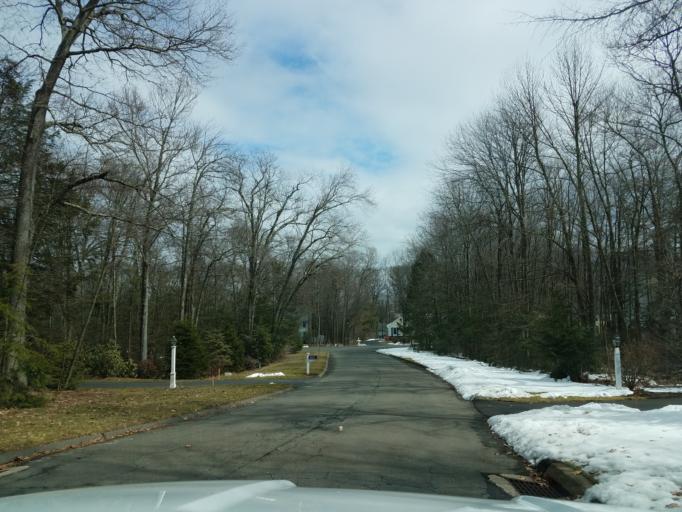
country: US
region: Connecticut
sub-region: Hartford County
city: Canton Valley
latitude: 41.7941
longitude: -72.8754
